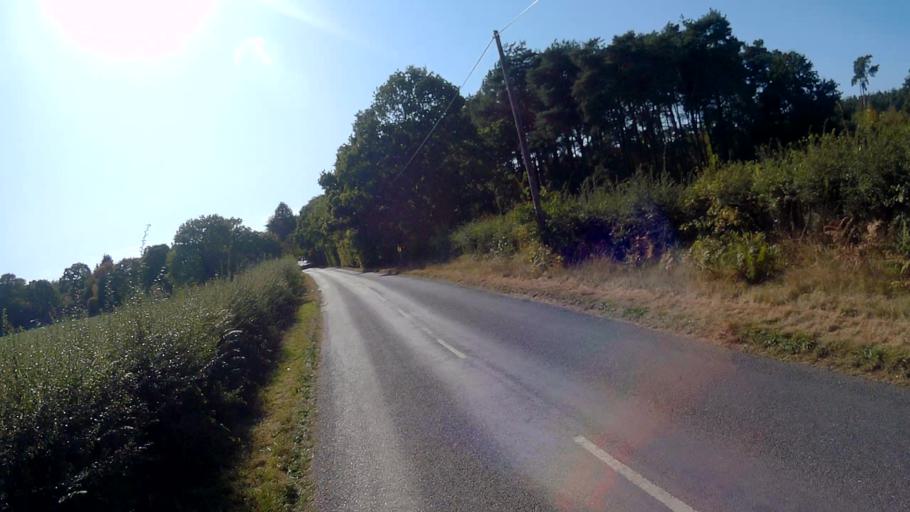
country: GB
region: England
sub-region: Surrey
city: Farnham
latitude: 51.1810
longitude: -0.7750
